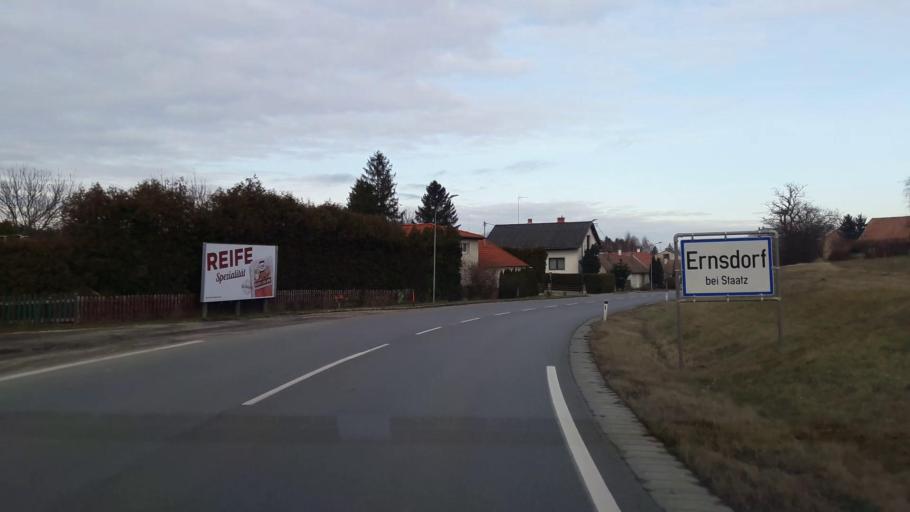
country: AT
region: Lower Austria
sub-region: Politischer Bezirk Mistelbach
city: Staatz
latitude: 48.6579
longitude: 16.4966
